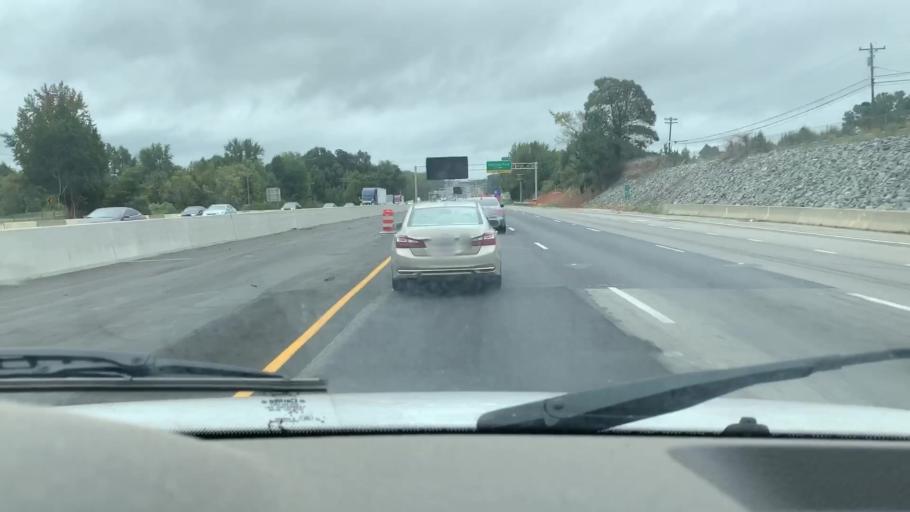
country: US
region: North Carolina
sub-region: Gaston County
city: Davidson
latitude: 35.5491
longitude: -80.8584
